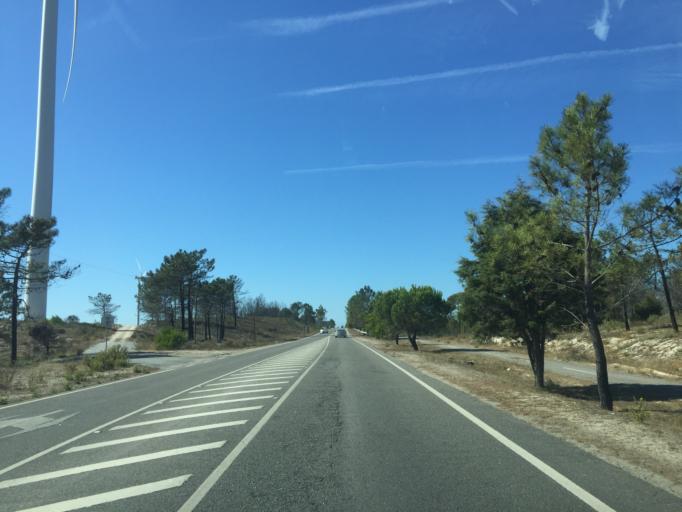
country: PT
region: Coimbra
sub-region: Mira
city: Mira
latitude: 40.3249
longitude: -8.8089
